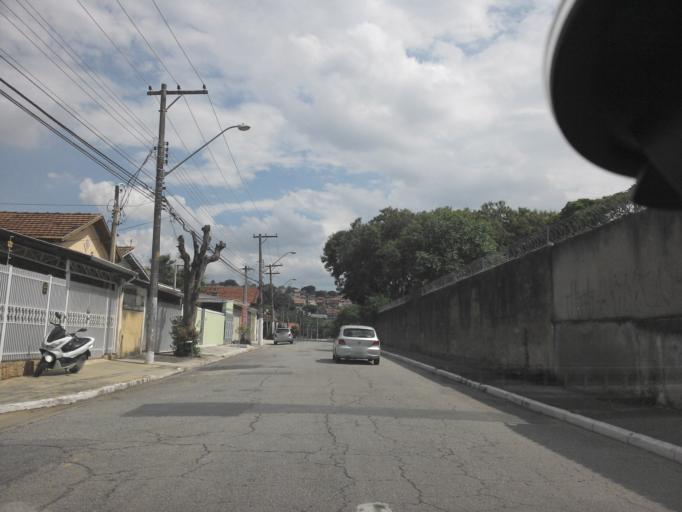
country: BR
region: Sao Paulo
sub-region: Taubate
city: Taubate
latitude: -23.0381
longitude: -45.5726
